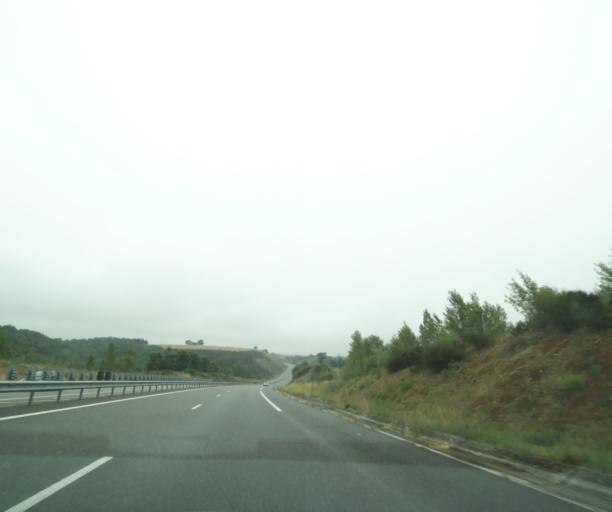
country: FR
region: Midi-Pyrenees
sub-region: Departement du Tarn
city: Carmaux
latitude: 44.0660
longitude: 2.2186
